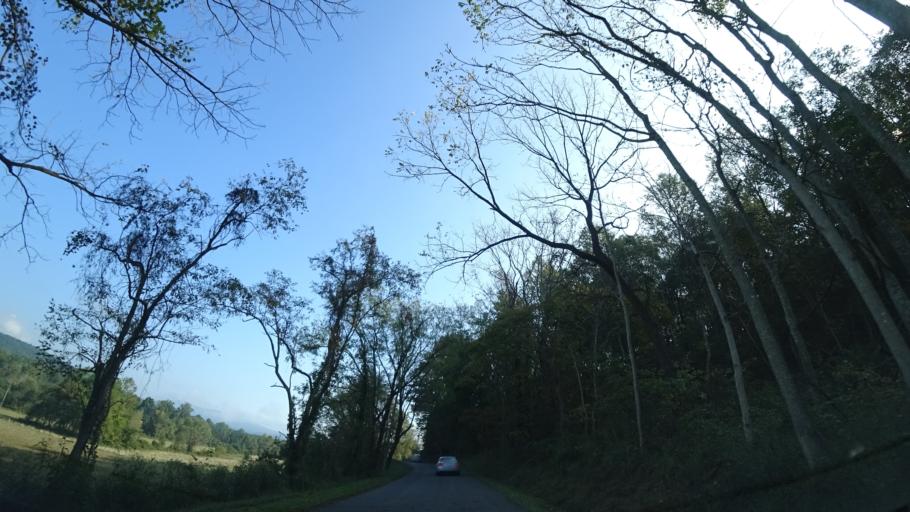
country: US
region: Virginia
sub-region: Madison County
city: Brightwood
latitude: 38.5223
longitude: -78.2832
